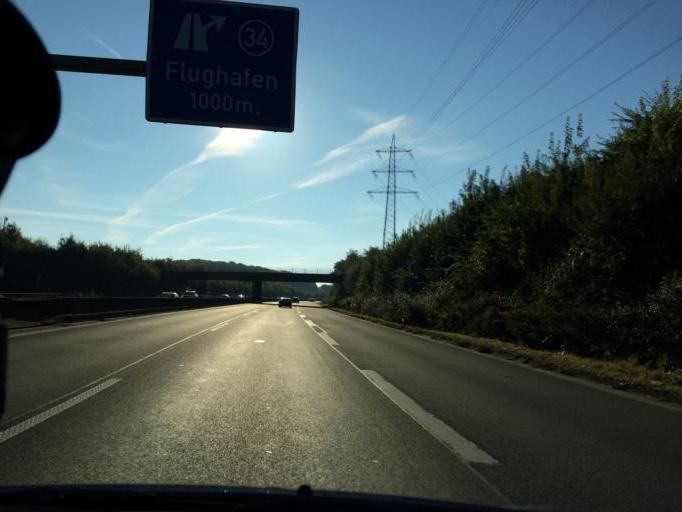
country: DE
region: North Rhine-Westphalia
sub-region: Regierungsbezirk Koln
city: Eil
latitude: 50.8975
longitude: 7.0850
